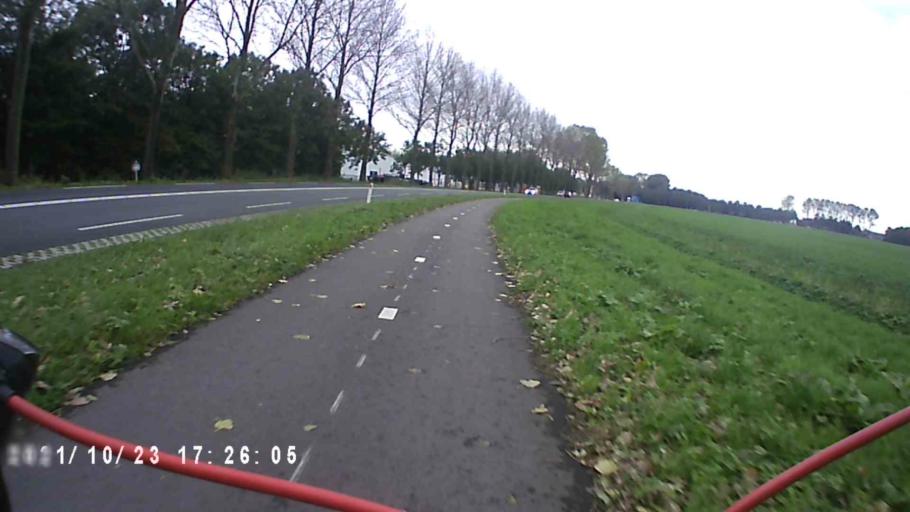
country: NL
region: North Holland
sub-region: Gemeente Medemblik
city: Opperdoes
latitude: 52.8378
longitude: 5.0244
